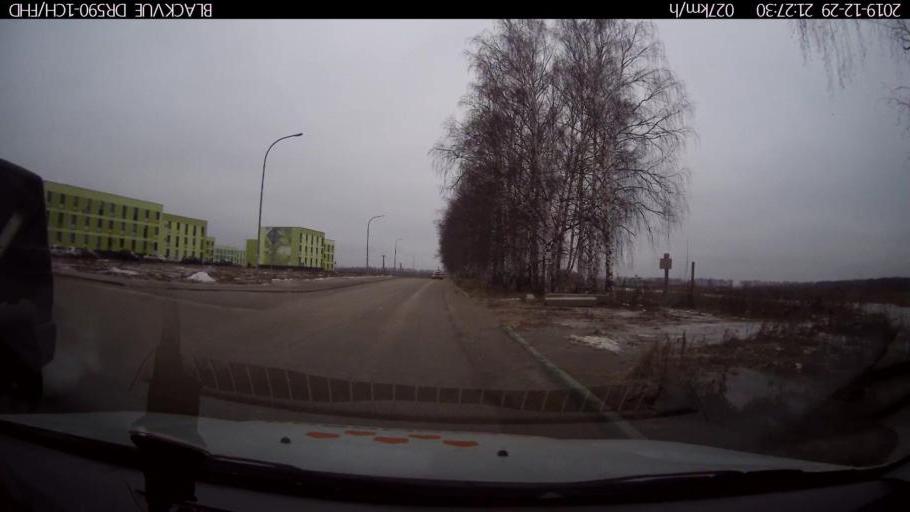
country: RU
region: Nizjnij Novgorod
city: Afonino
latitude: 56.2129
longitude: 44.0224
